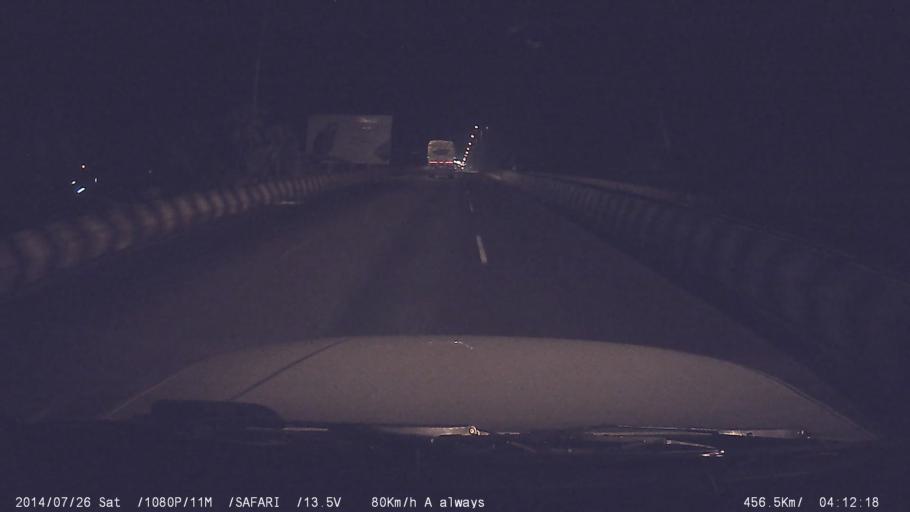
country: IN
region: Kerala
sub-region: Thrissur District
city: Trichur
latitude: 10.4943
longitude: 76.2581
